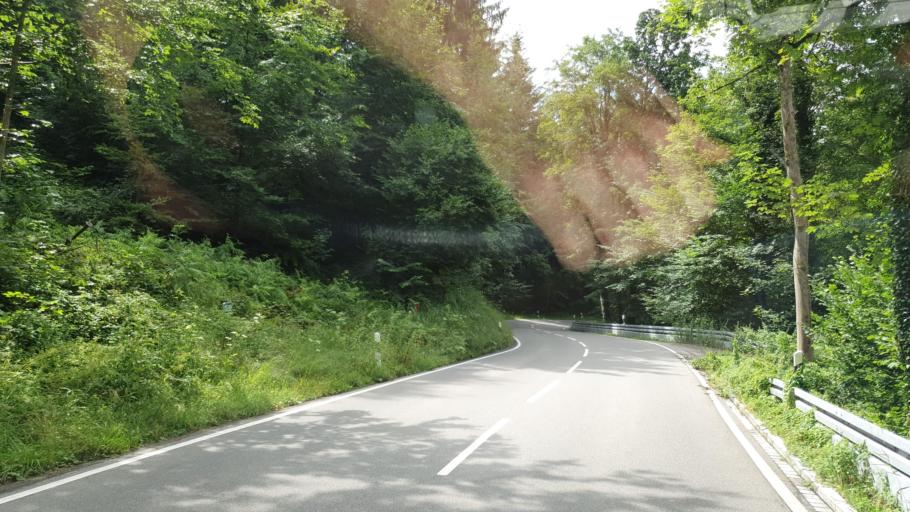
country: AT
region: Vorarlberg
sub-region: Politischer Bezirk Bregenz
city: Moggers
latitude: 47.5938
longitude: 9.8141
